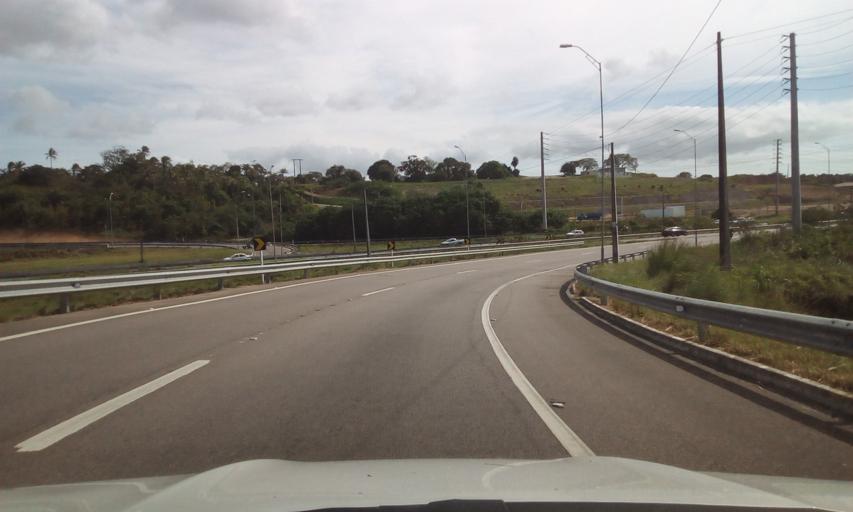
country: BR
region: Paraiba
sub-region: Bayeux
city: Bayeux
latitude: -7.1492
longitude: -34.9107
